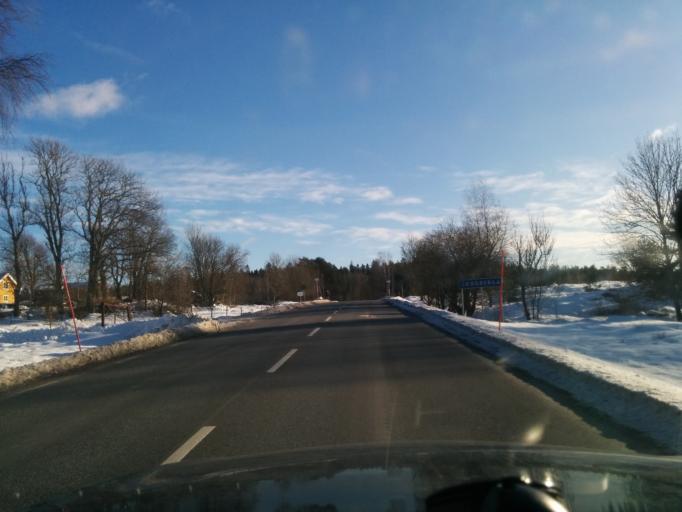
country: SE
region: Stockholm
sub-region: Taby Kommun
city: Taby
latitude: 59.4853
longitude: 18.0855
